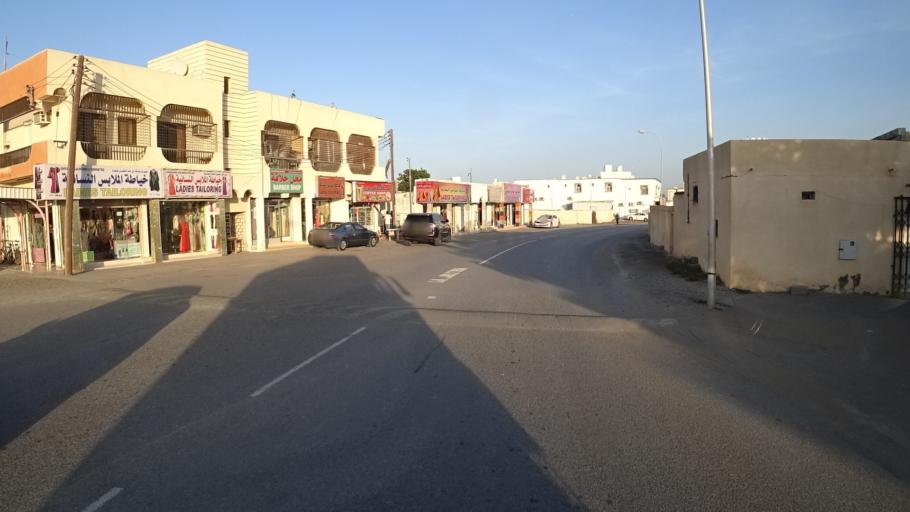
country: OM
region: Al Batinah
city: Barka'
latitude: 23.7072
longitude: 57.8969
